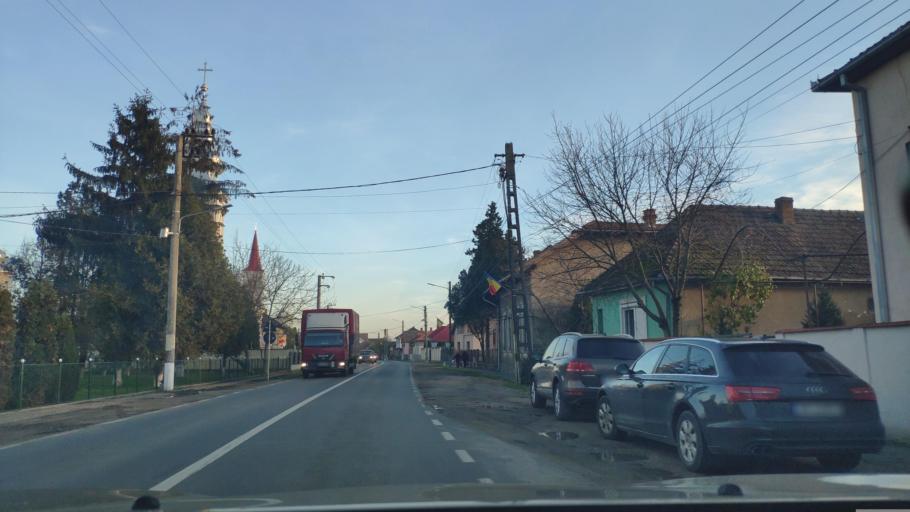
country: RO
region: Satu Mare
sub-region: Comuna Odoreu
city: Odoreu
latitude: 47.7948
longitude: 22.9926
